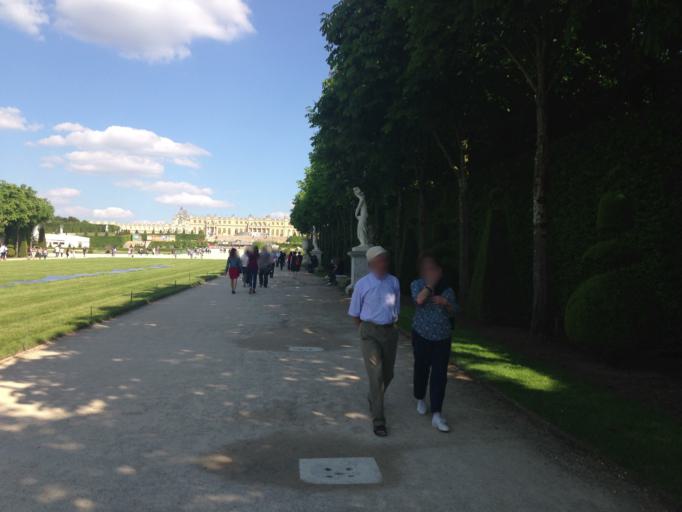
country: FR
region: Ile-de-France
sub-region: Departement des Yvelines
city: Le Chesnay
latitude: 48.8060
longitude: 2.1148
